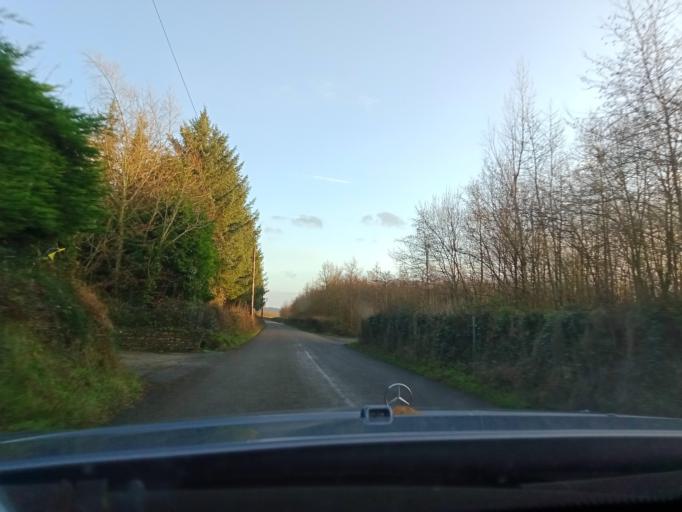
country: IE
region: Leinster
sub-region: Kilkenny
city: Callan
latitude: 52.4980
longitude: -7.3370
